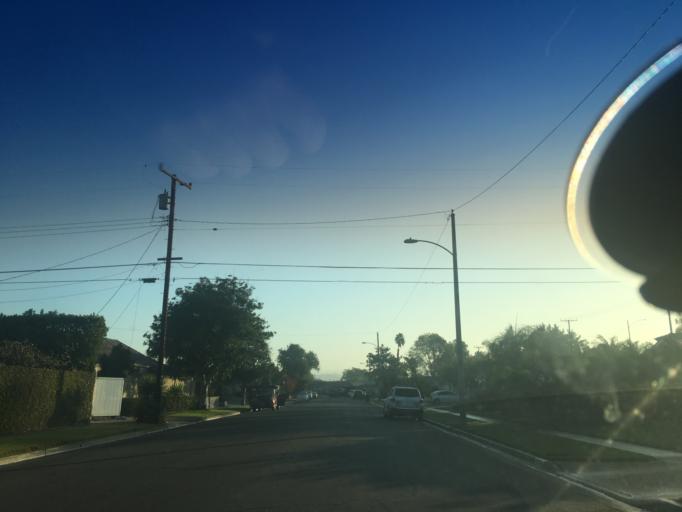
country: US
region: California
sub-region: Orange County
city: Anaheim
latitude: 33.8260
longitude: -117.8782
